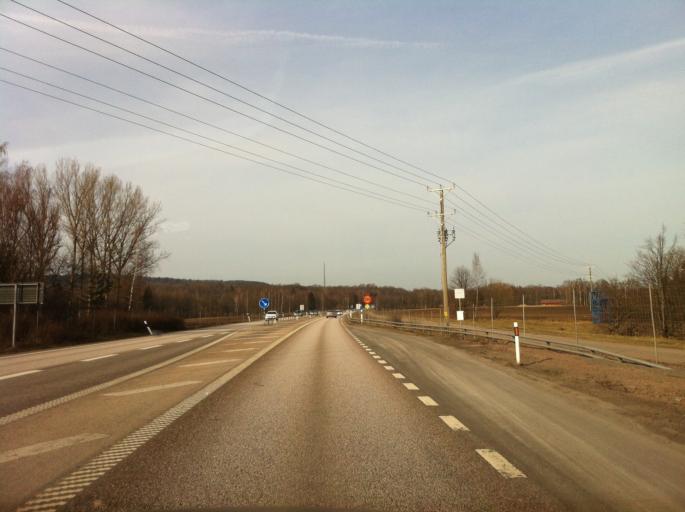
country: SE
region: Vaestra Goetaland
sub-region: Skovde Kommun
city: Stopen
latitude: 58.4436
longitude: 13.8535
